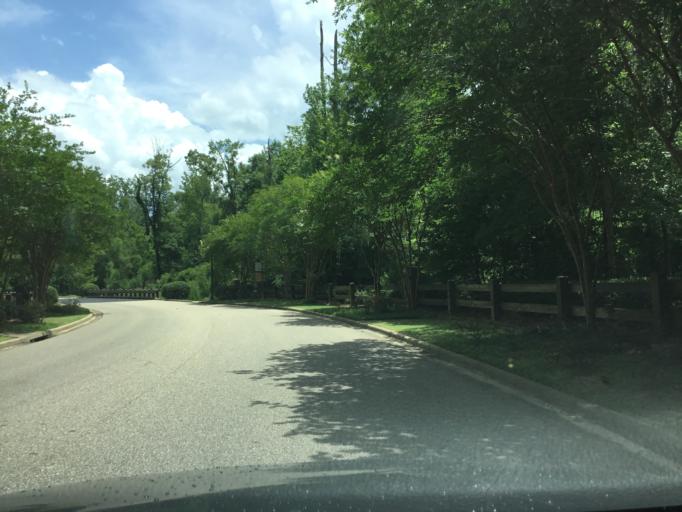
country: US
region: Alabama
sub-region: Montgomery County
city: Pike Road
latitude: 32.3461
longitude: -86.0852
